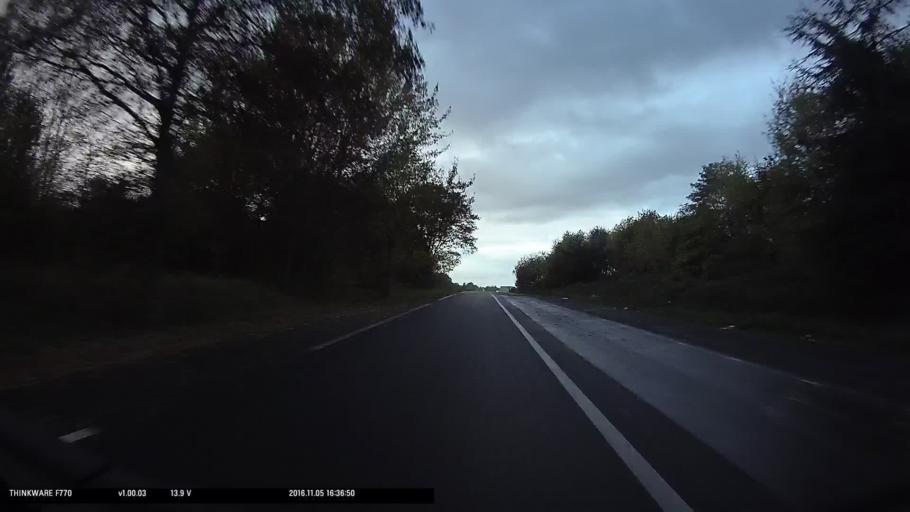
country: FR
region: Ile-de-France
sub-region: Departement du Val-d'Oise
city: Courdimanche
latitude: 49.0569
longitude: 2.0080
